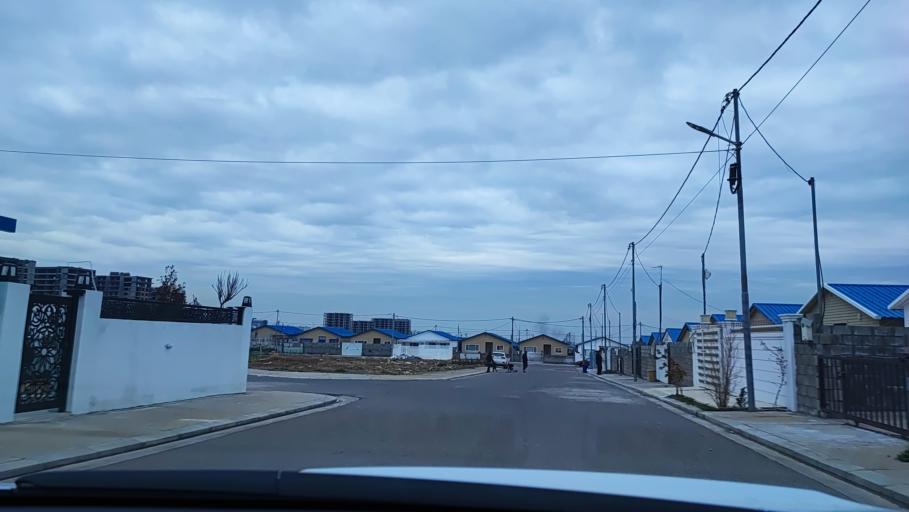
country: IQ
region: Arbil
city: Erbil
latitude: 36.2863
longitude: 44.0815
